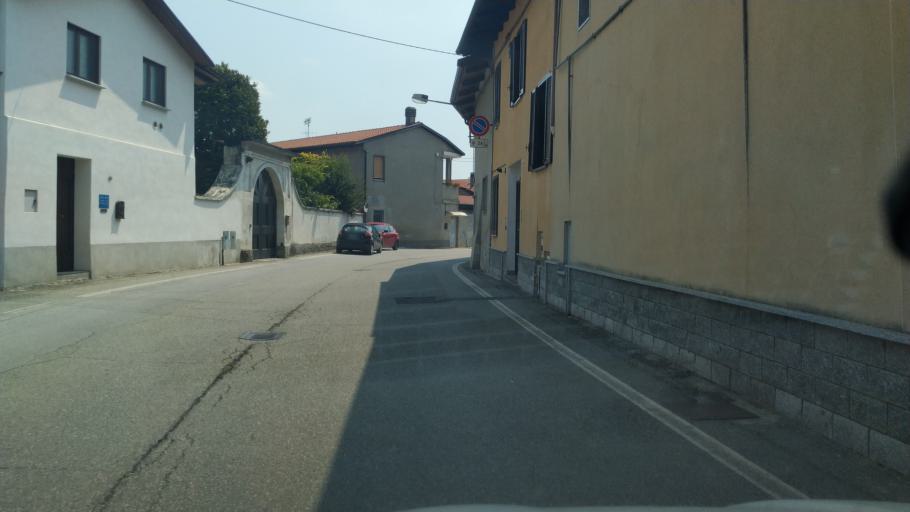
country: IT
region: Piedmont
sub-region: Provincia di Torino
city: Rondissone
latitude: 45.2447
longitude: 7.9671
